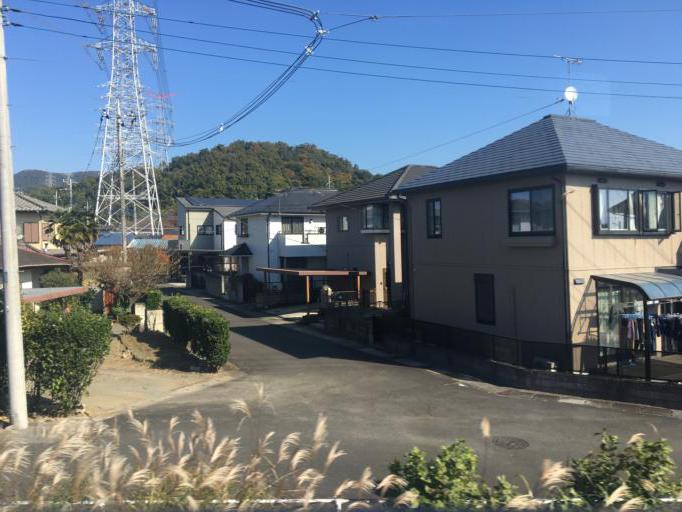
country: JP
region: Gunma
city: Kiryu
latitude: 36.3696
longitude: 139.3813
